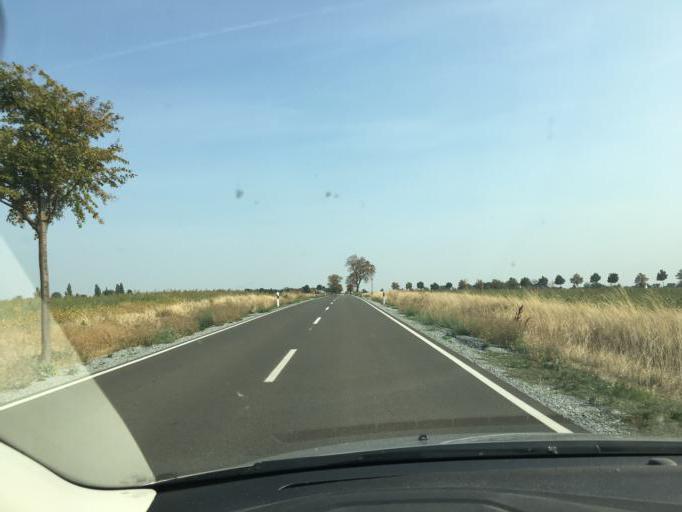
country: DE
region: Saxony-Anhalt
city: Wulfen
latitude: 51.7919
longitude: 11.8714
